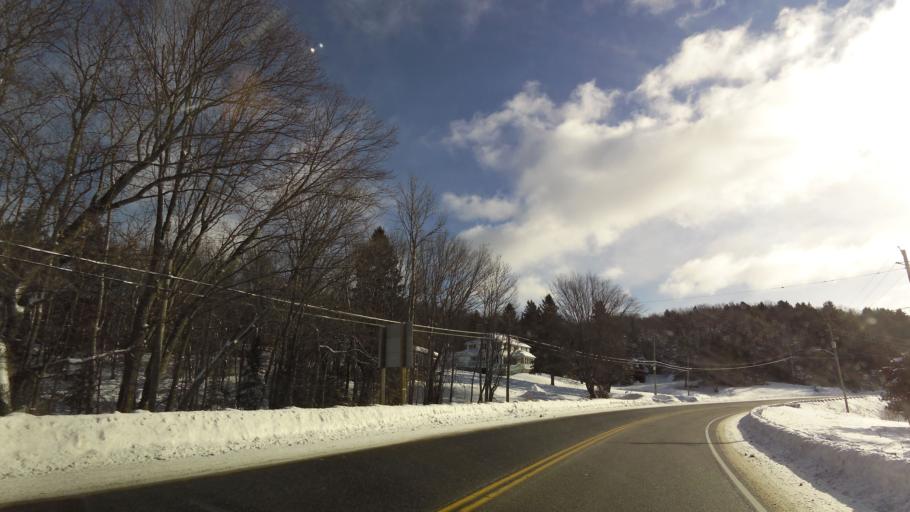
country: CA
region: Ontario
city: Bancroft
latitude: 45.0560
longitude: -78.5142
